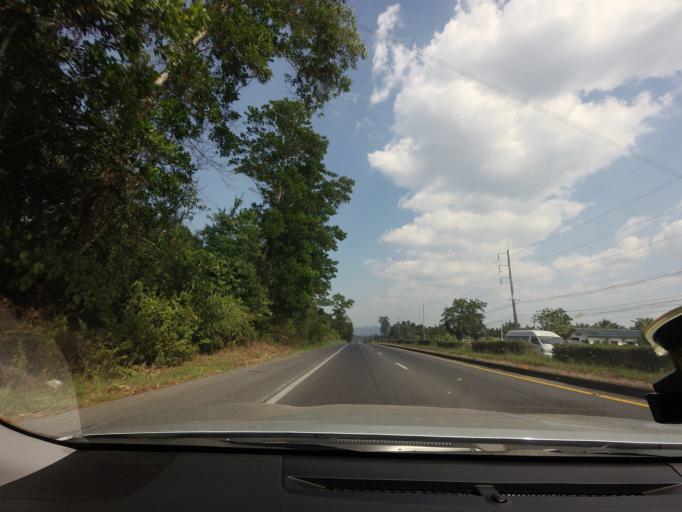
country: TH
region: Phangnga
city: Thap Put
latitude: 8.5078
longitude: 98.6706
